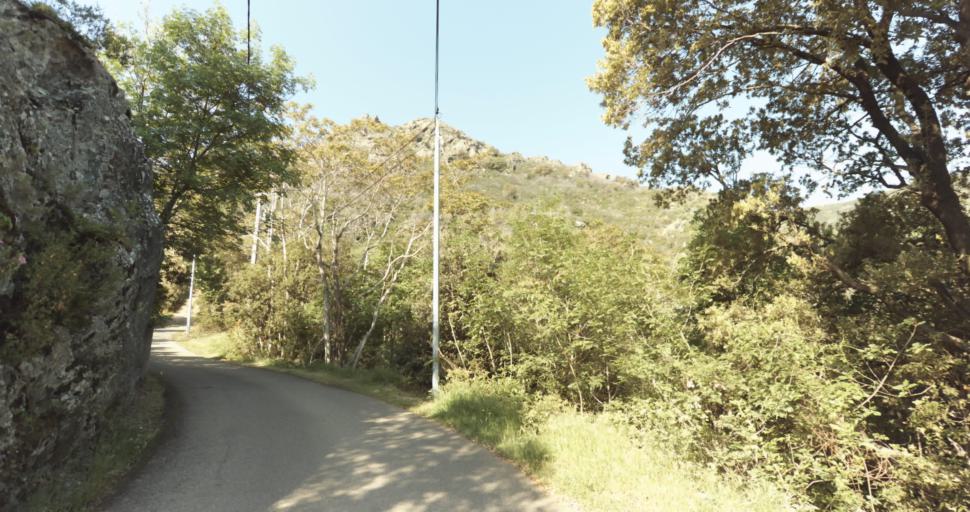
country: FR
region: Corsica
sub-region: Departement de la Haute-Corse
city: Biguglia
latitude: 42.6315
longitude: 9.4177
